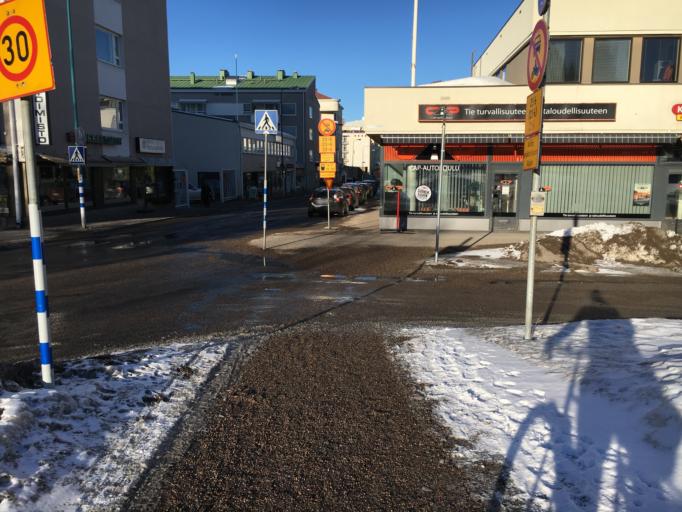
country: FI
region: Kainuu
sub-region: Kajaani
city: Kajaani
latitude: 64.2257
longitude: 27.7290
